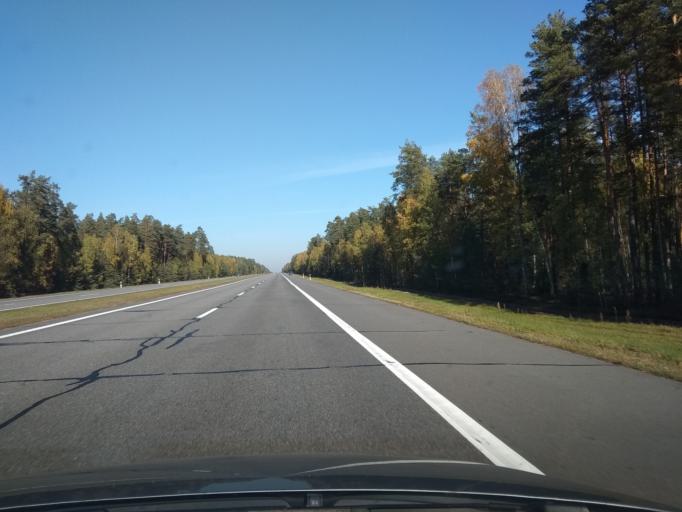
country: BY
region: Grodnenskaya
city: Zhyrovichy
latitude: 52.8772
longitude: 25.6616
